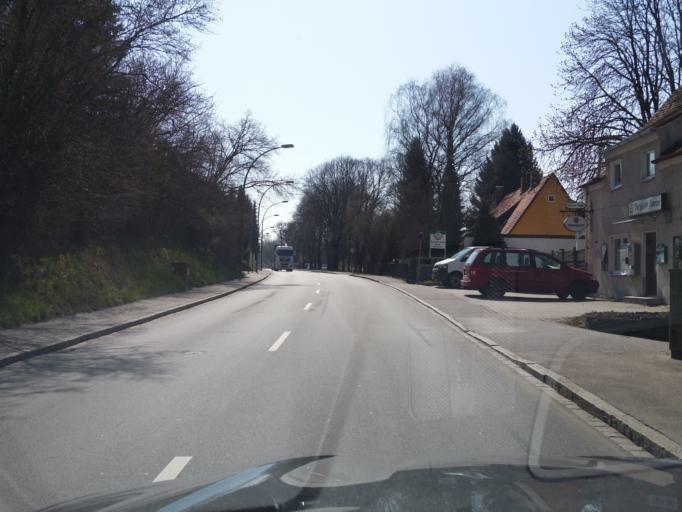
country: DE
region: Bavaria
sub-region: Lower Bavaria
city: Landshut
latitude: 48.5159
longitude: 12.1529
